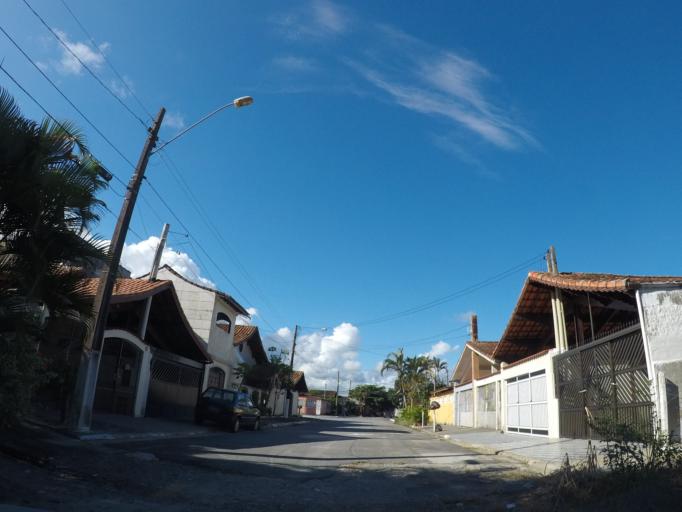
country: BR
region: Sao Paulo
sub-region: Mongagua
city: Mongagua
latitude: -24.0567
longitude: -46.5425
